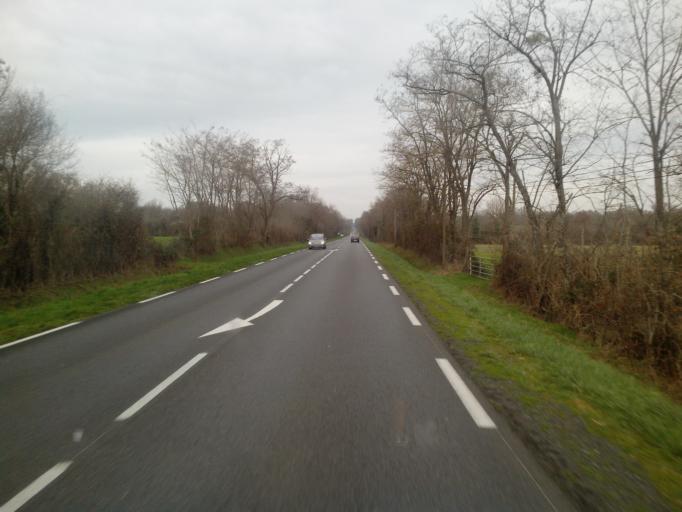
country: FR
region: Poitou-Charentes
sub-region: Departement de la Vienne
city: Saulge
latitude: 46.3405
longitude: 0.8000
